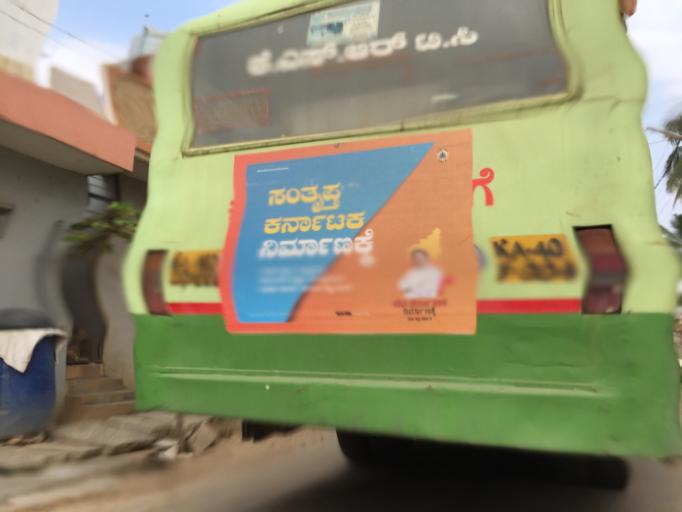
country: IN
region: Karnataka
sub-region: Chikkaballapur
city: Chik Ballapur
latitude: 13.4282
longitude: 77.7250
